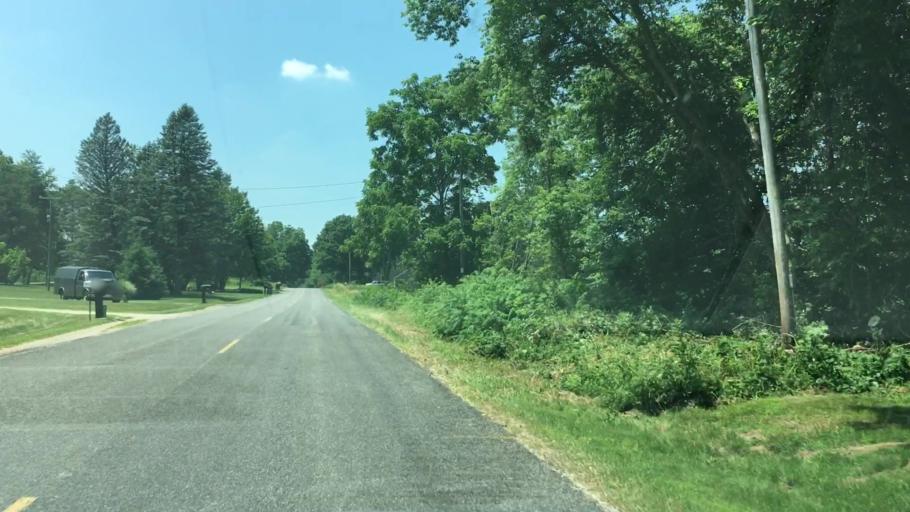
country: US
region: Michigan
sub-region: Kent County
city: Byron Center
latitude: 42.8414
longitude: -85.7655
